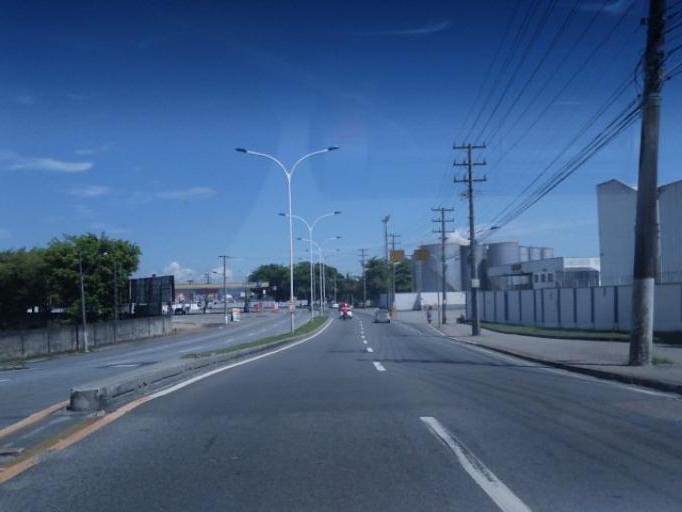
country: BR
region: Santa Catarina
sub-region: Itajai
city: Itajai
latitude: -26.8894
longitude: -48.6844
